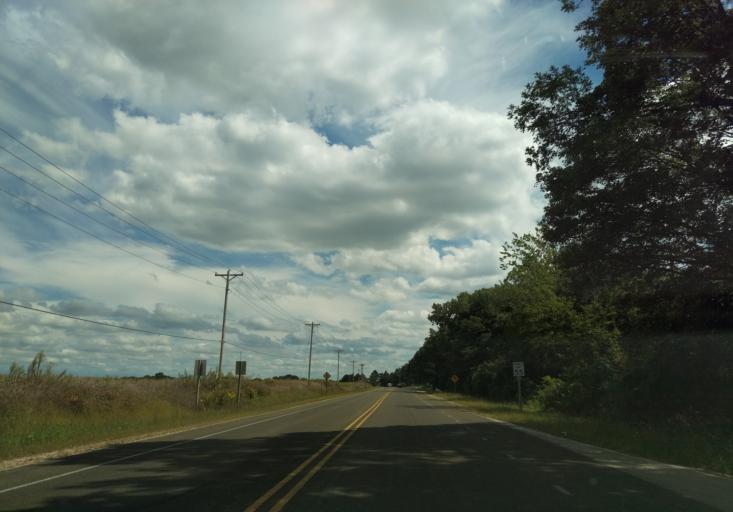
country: US
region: Wisconsin
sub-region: Dane County
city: Shorewood Hills
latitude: 43.1192
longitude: -89.4495
